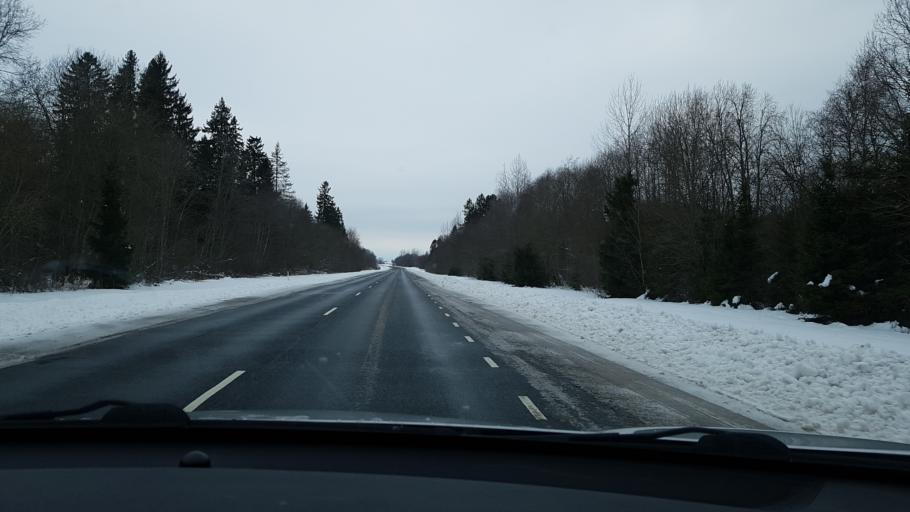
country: EE
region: Jaervamaa
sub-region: Jaerva-Jaani vald
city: Jarva-Jaani
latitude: 58.8968
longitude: 25.7819
